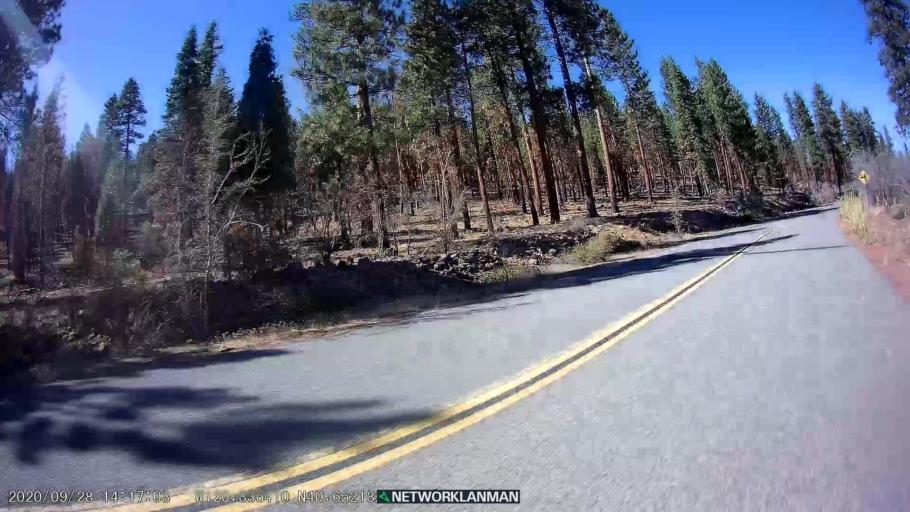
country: US
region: California
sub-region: Lassen County
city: Susanville
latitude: 40.6524
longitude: -120.8365
